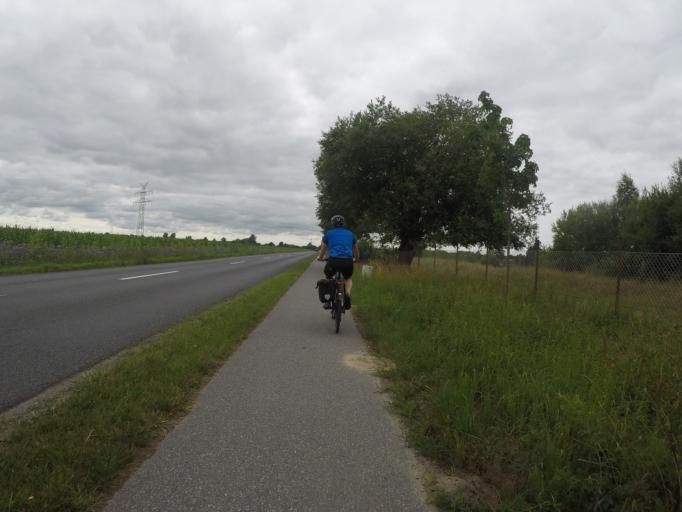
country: DE
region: Lower Saxony
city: Hemmoor
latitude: 53.6933
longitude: 9.1389
